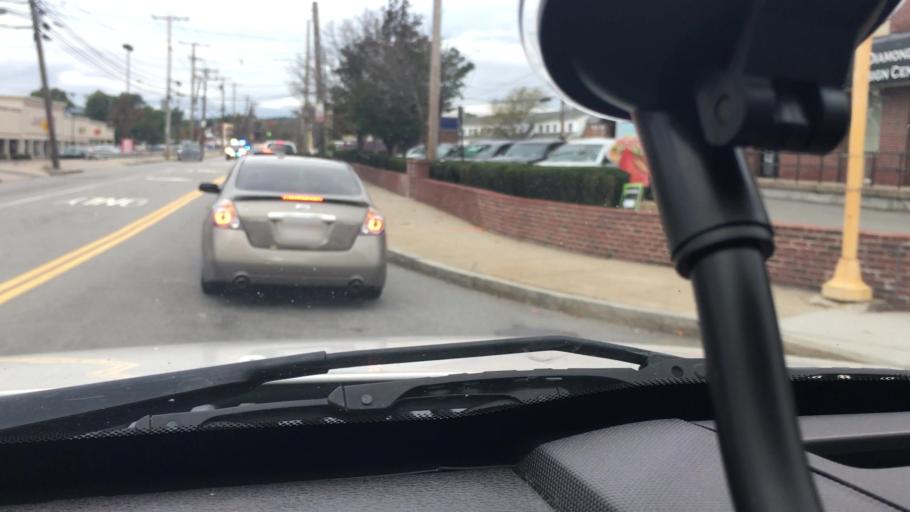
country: US
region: Massachusetts
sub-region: Middlesex County
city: Waltham
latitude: 42.3685
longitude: -71.2176
